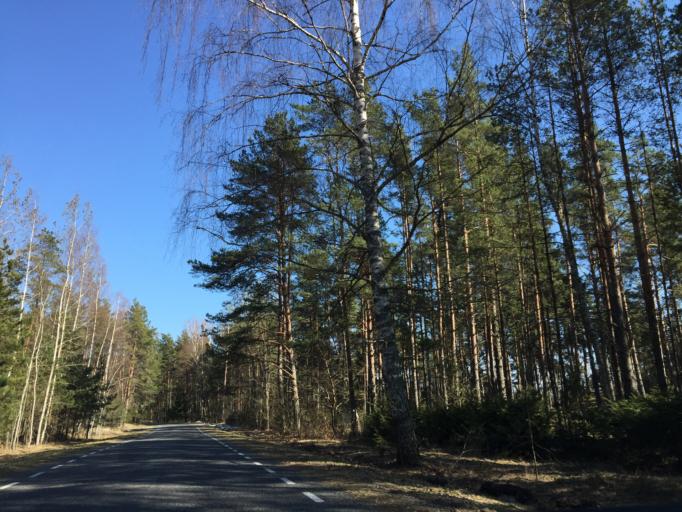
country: EE
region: Ida-Virumaa
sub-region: Johvi vald
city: Johvi
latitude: 59.0070
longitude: 27.4019
